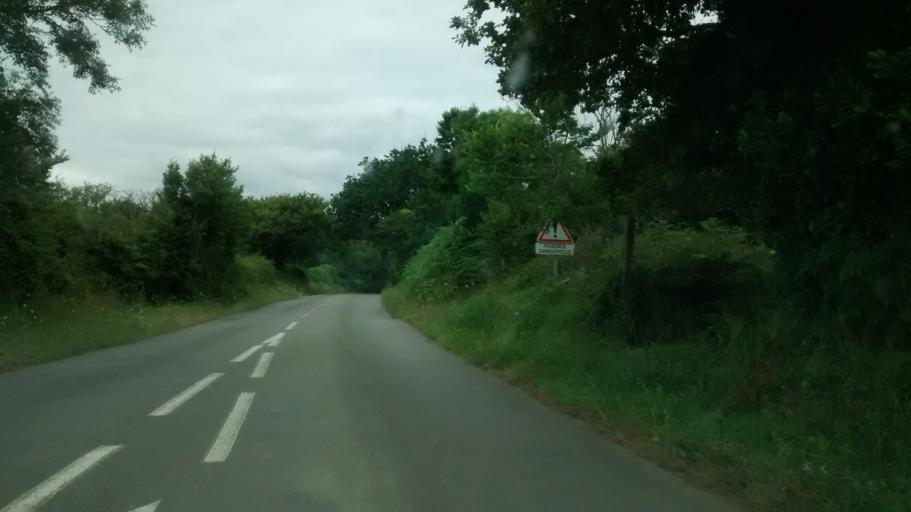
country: FR
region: Brittany
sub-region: Departement du Finistere
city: Plougastel-Daoulas
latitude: 48.3353
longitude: -4.3907
